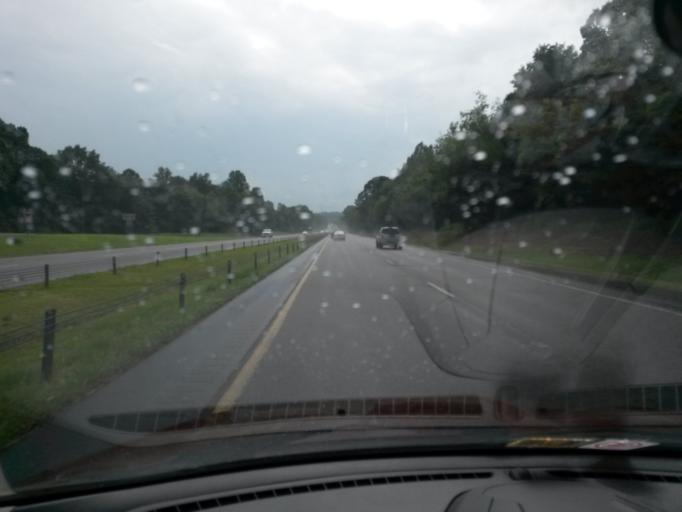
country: US
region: North Carolina
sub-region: Alexander County
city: Stony Point
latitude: 35.7643
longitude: -81.0212
